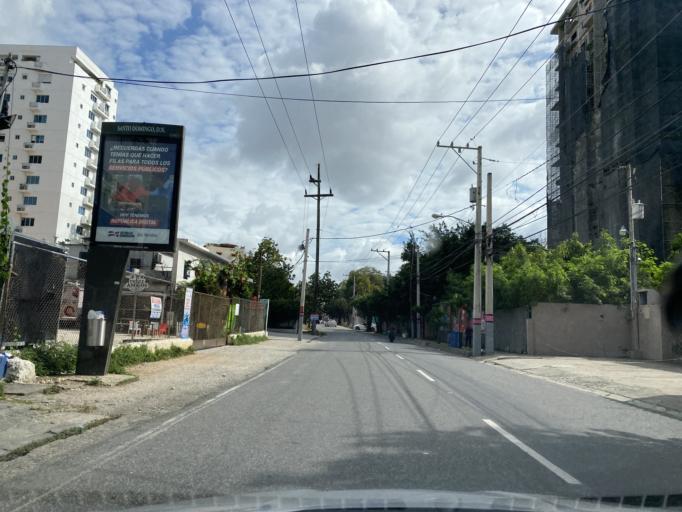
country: DO
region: Nacional
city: La Julia
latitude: 18.4755
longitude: -69.9254
